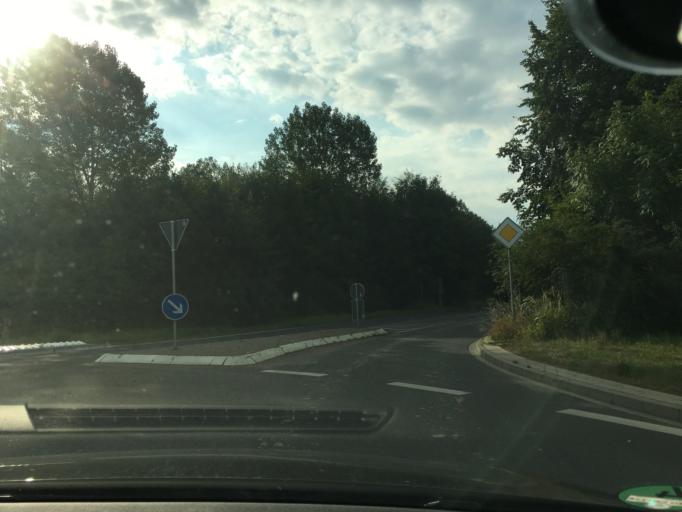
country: DE
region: North Rhine-Westphalia
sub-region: Regierungsbezirk Koln
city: Inden
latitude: 50.8491
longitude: 6.4144
